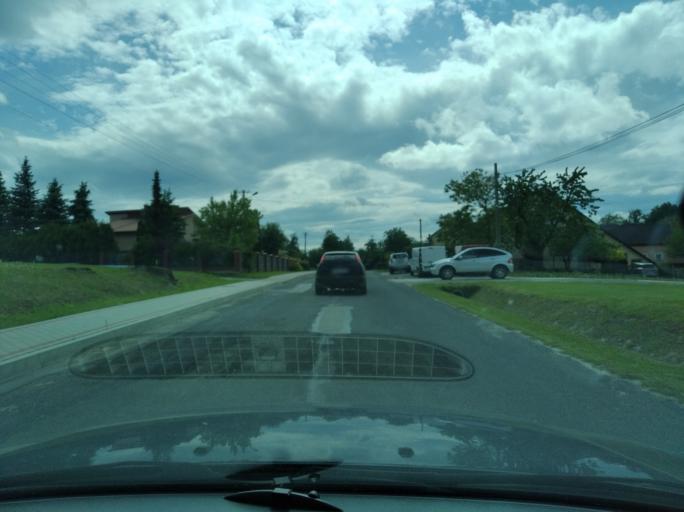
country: PL
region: Subcarpathian Voivodeship
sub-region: Powiat ropczycko-sedziszowski
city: Ropczyce
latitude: 50.0301
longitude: 21.6119
